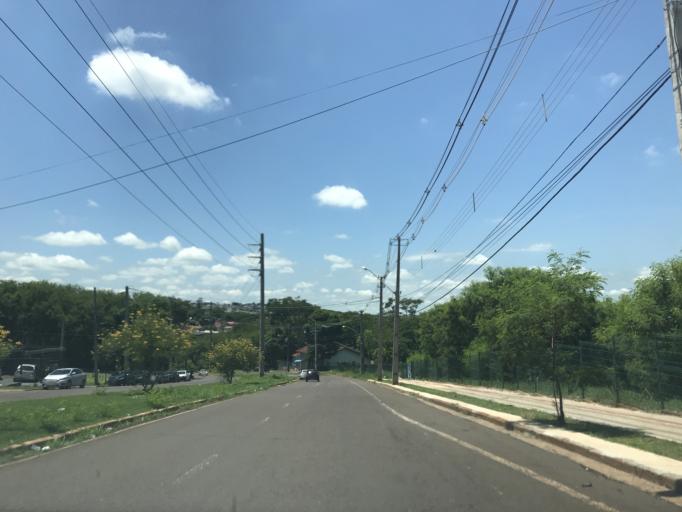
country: BR
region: Parana
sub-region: Maringa
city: Maringa
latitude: -23.4524
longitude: -51.9319
